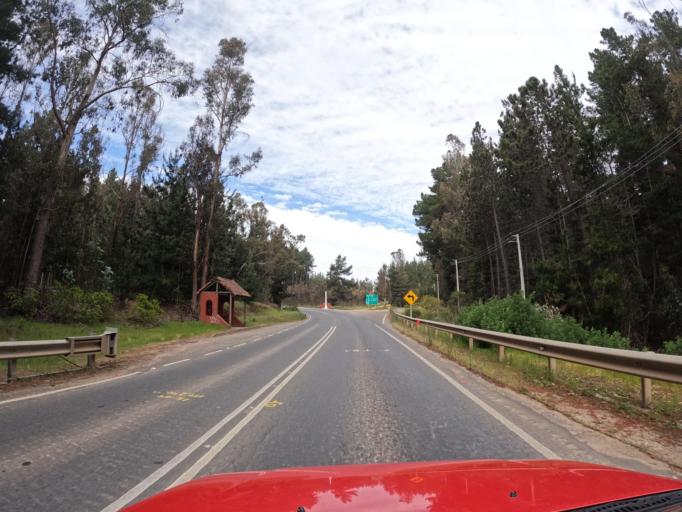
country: CL
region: O'Higgins
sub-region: Provincia de Colchagua
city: Santa Cruz
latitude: -34.3570
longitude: -71.8691
